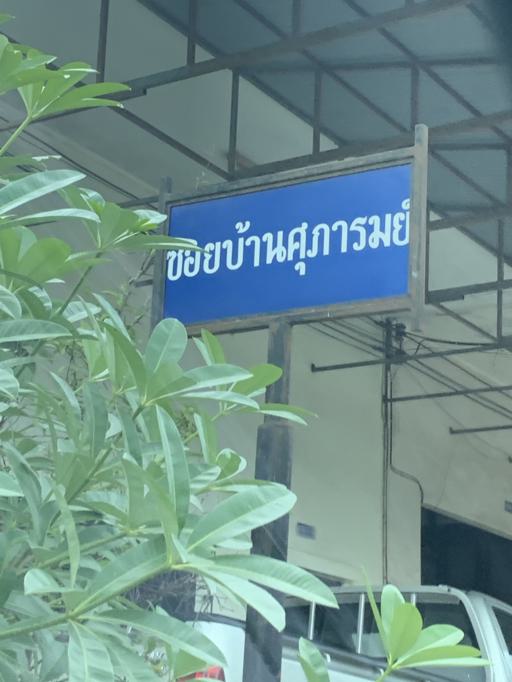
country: TH
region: Yala
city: Yala
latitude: 6.5301
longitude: 101.2923
